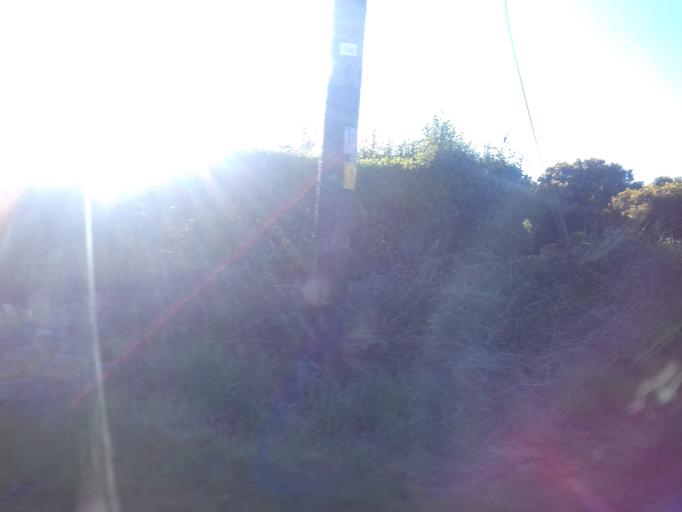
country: IE
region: Leinster
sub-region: Fingal County
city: Howth
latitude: 53.3744
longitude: -6.0646
